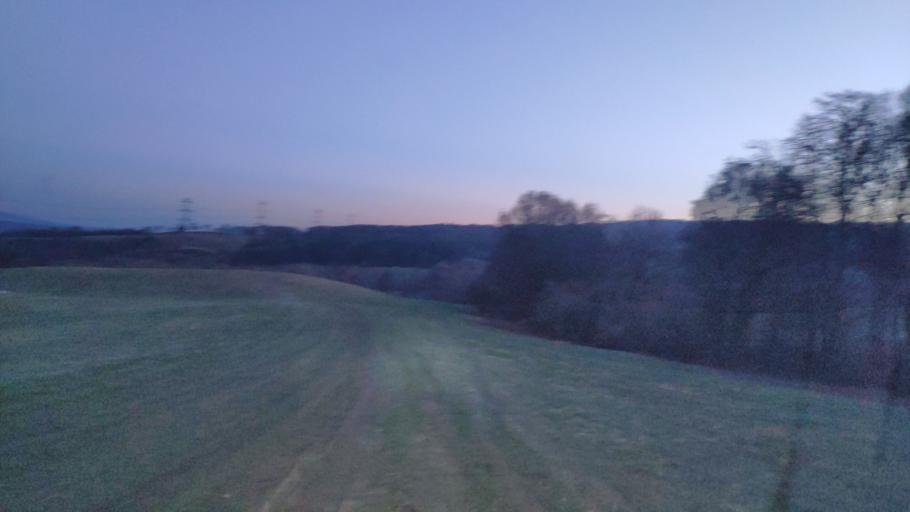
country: SK
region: Kosicky
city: Kosice
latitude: 48.8249
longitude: 21.2648
